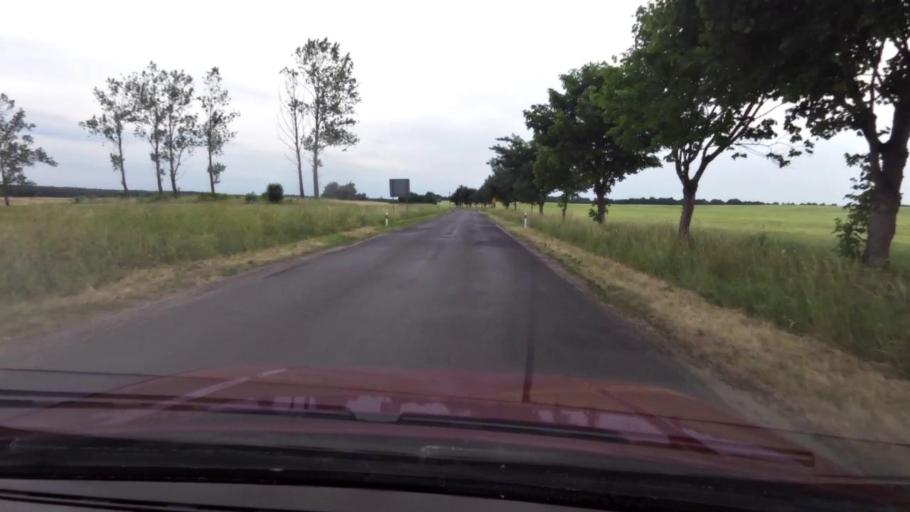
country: PL
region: Pomeranian Voivodeship
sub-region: Powiat bytowski
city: Trzebielino
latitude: 54.2750
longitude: 17.0887
